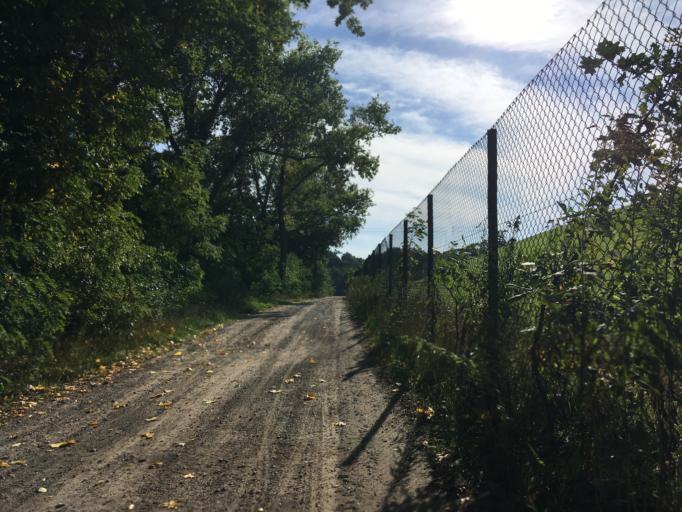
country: DE
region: Brandenburg
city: Neuenhagen
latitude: 52.5251
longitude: 13.7188
